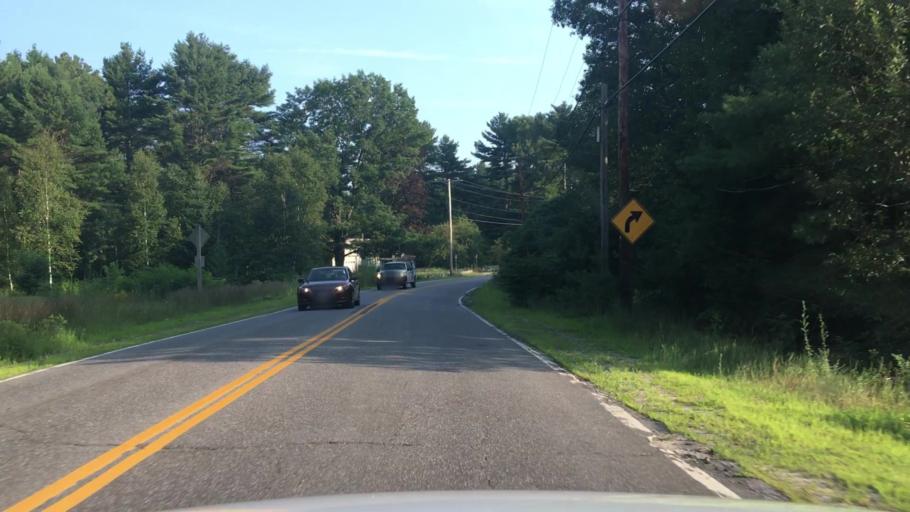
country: US
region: Maine
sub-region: Androscoggin County
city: Lisbon Falls
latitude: 43.9892
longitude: -70.0530
